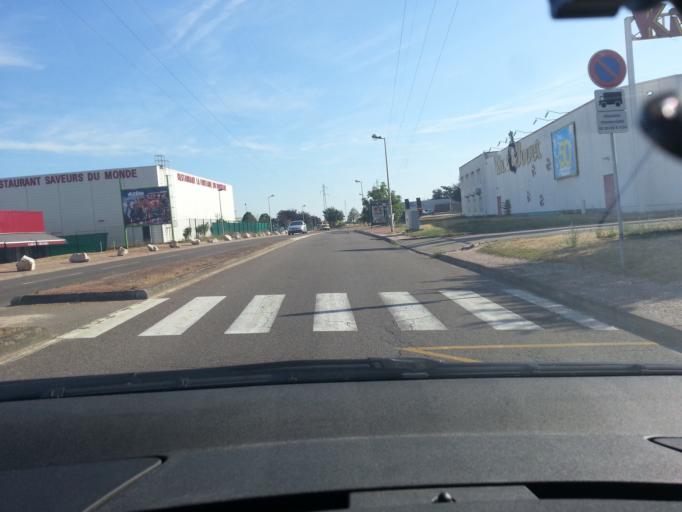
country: FR
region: Bourgogne
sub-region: Departement de la Cote-d'Or
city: Perrigny-les-Dijon
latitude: 47.2790
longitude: 5.0165
